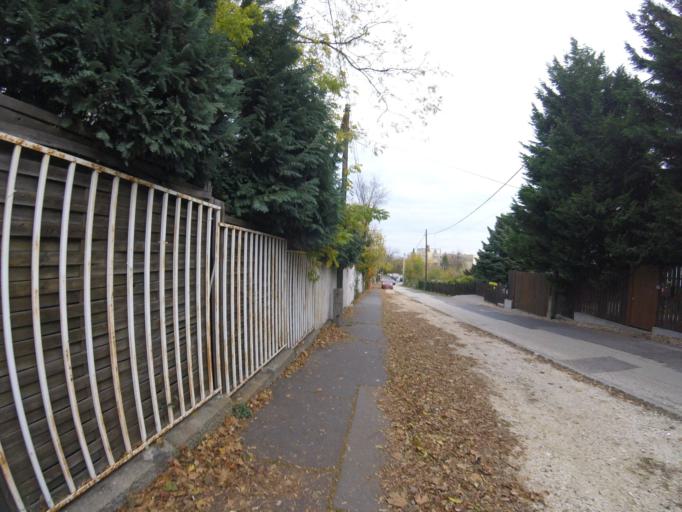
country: HU
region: Budapest
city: Budapest XII. keruelet
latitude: 47.4948
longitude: 18.9812
